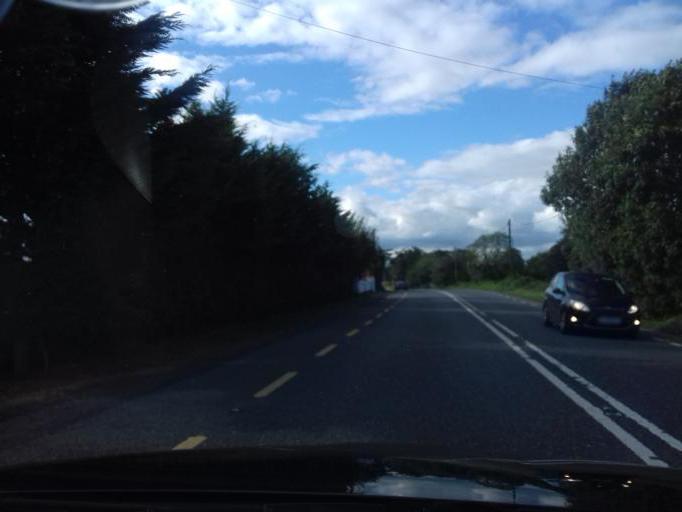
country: IE
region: Leinster
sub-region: Uibh Fhaili
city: Tullamore
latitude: 53.3130
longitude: -7.5048
